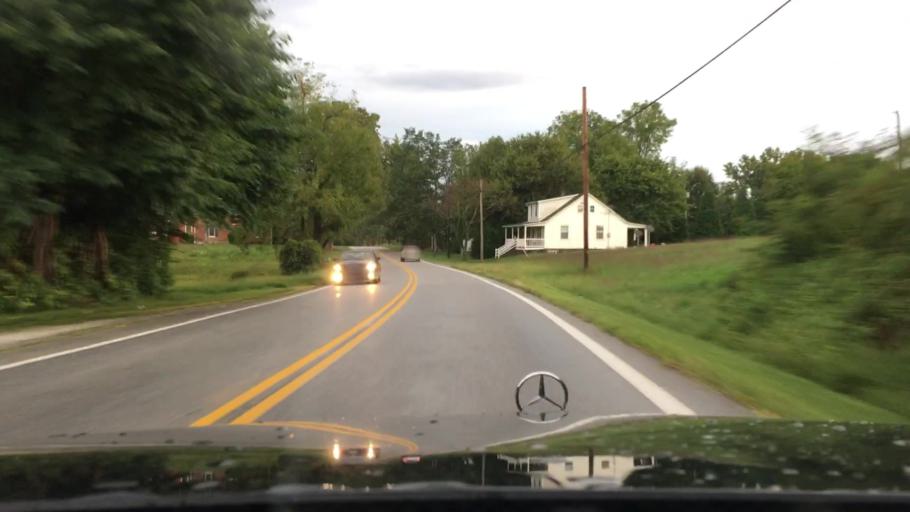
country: US
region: Virginia
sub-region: Amherst County
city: Amherst
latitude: 37.6415
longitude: -79.0227
